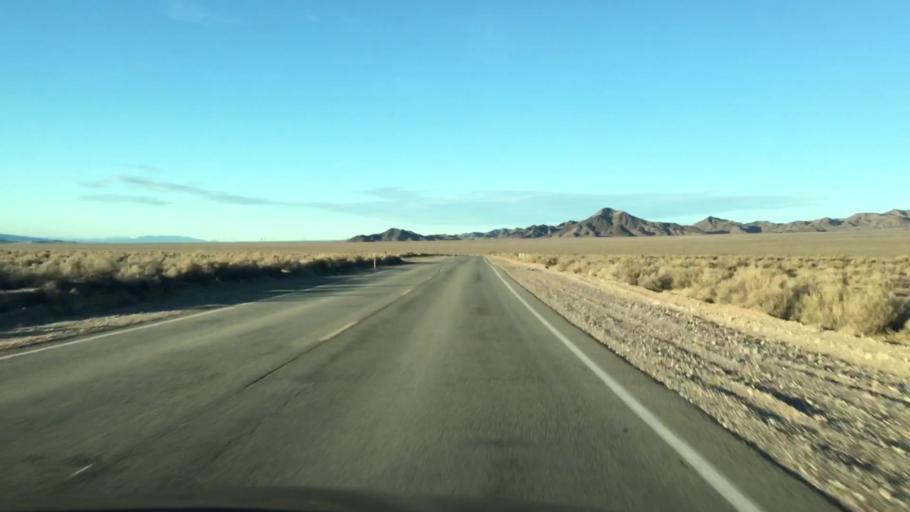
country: US
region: California
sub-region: San Bernardino County
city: Fort Irwin
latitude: 35.3353
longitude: -116.0820
